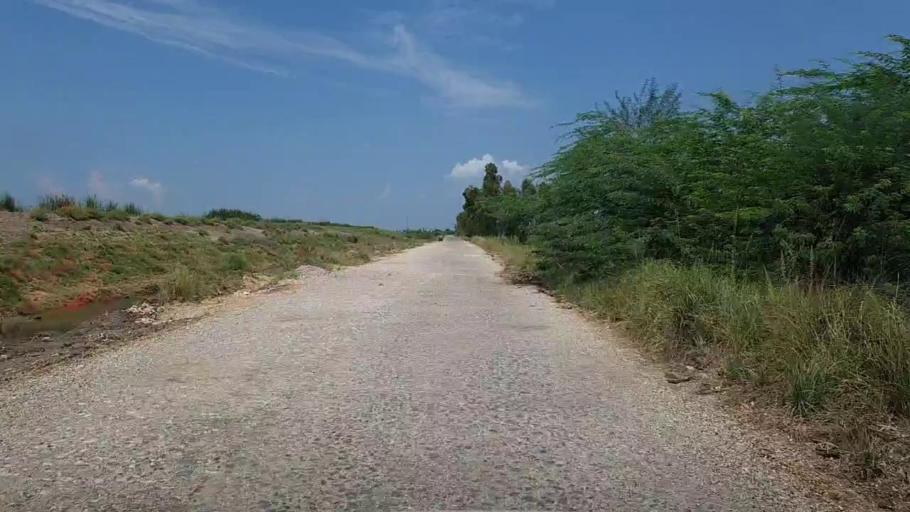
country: PK
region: Sindh
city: Bhiria
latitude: 26.9161
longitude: 68.2058
